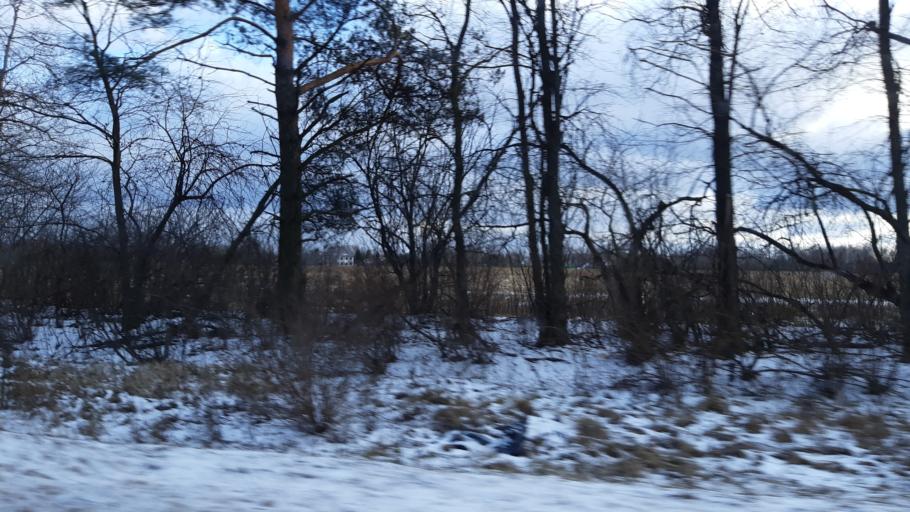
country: RU
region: Moskovskaya
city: Noginsk-9
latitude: 56.0063
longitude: 38.5562
